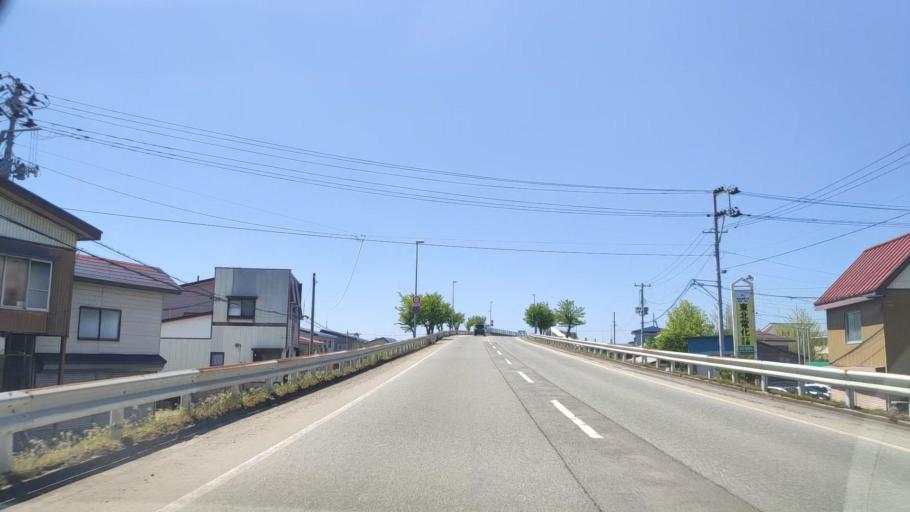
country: JP
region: Yamagata
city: Shinjo
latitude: 38.7711
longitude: 140.3070
